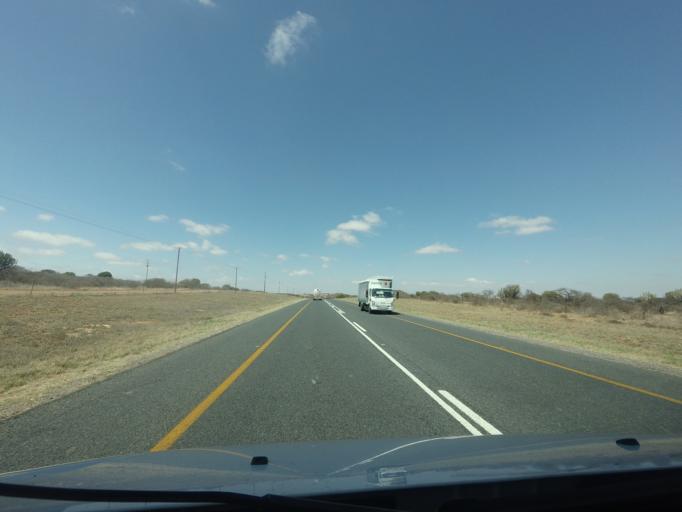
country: ZA
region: Limpopo
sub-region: Vhembe District Municipality
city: Louis Trichardt
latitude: -23.4228
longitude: 29.7507
